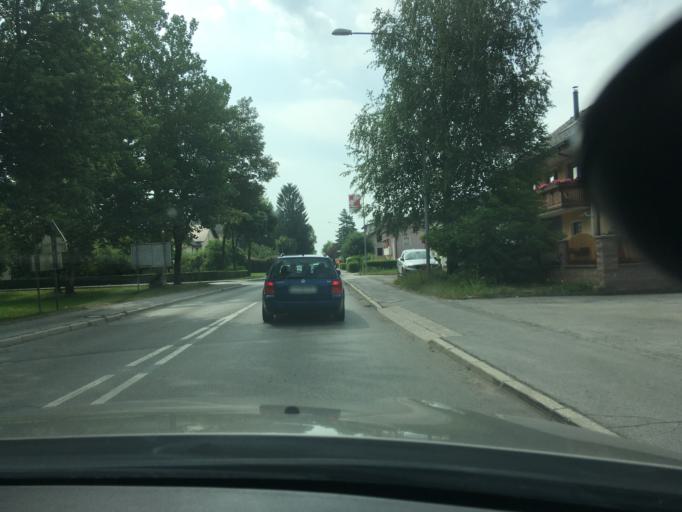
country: SI
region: Kocevje
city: Kocevje
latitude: 45.6442
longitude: 14.8534
